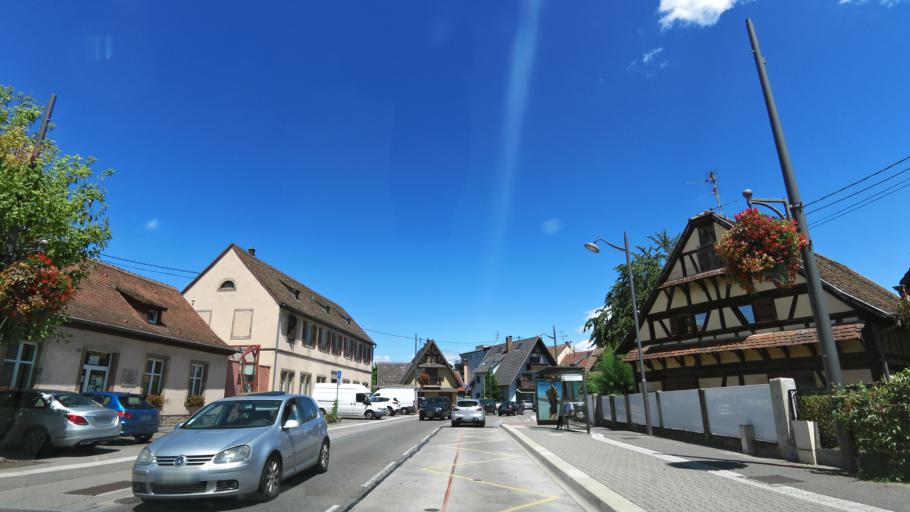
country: FR
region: Alsace
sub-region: Departement du Bas-Rhin
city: Illkirch-Graffenstaden
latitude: 48.5214
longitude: 7.7052
